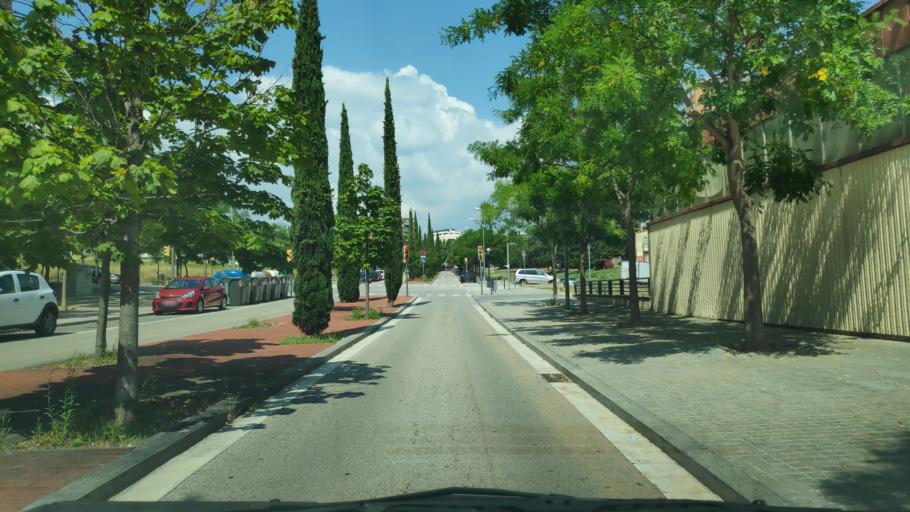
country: ES
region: Catalonia
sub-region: Provincia de Barcelona
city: Sant Quirze del Valles
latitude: 41.5472
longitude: 2.0839
